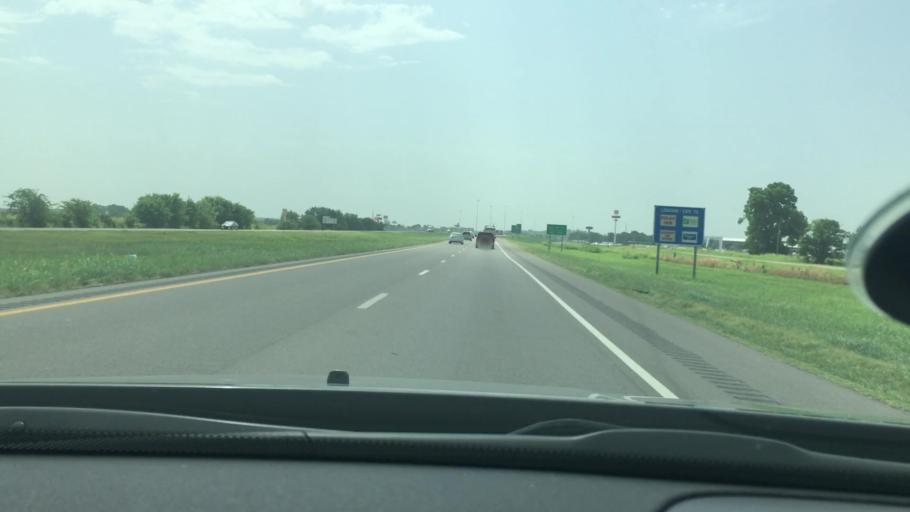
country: US
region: Oklahoma
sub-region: Garvin County
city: Pauls Valley
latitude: 34.7480
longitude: -97.2719
